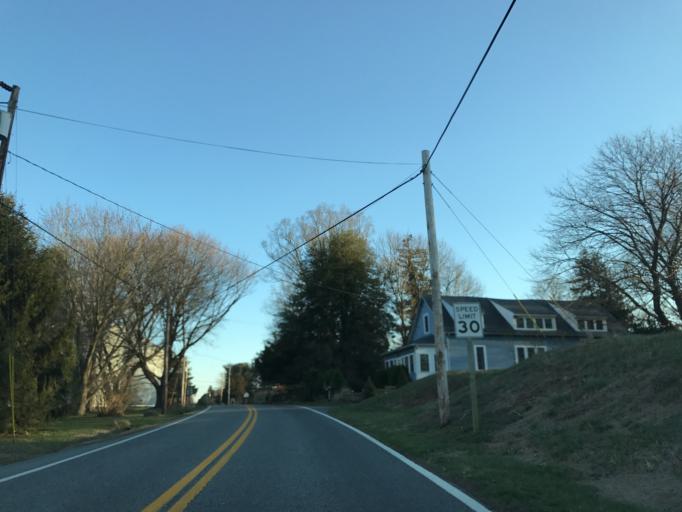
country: US
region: Maryland
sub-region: Queen Anne's County
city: Centreville
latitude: 38.9406
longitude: -76.0808
